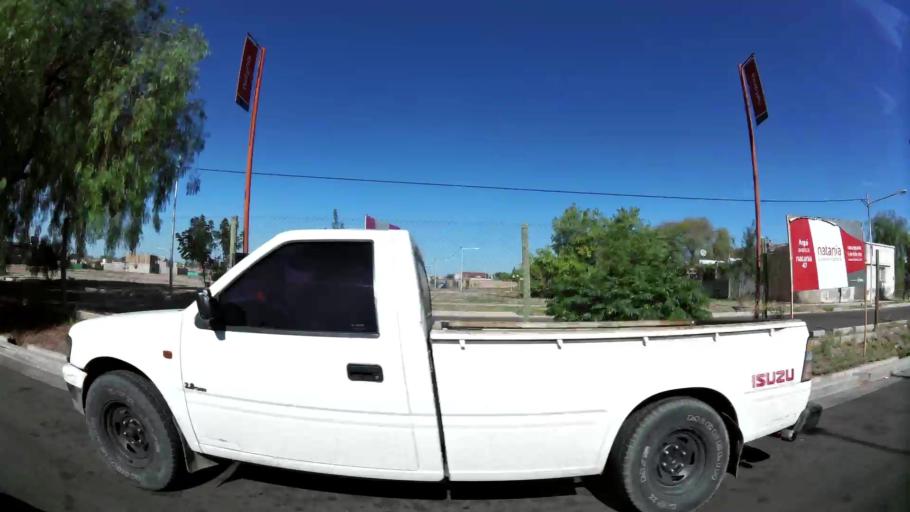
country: AR
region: Mendoza
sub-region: Departamento de Godoy Cruz
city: Godoy Cruz
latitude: -32.9427
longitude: -68.8046
